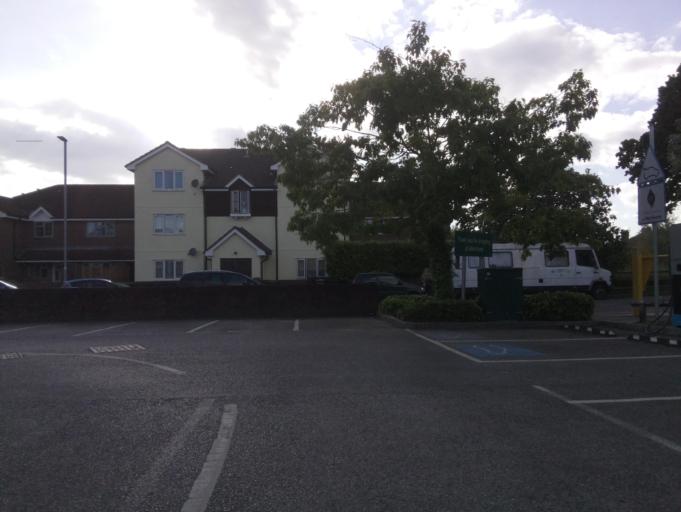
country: GB
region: England
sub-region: Somerset
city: Glastonbury
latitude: 51.1452
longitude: -2.7202
